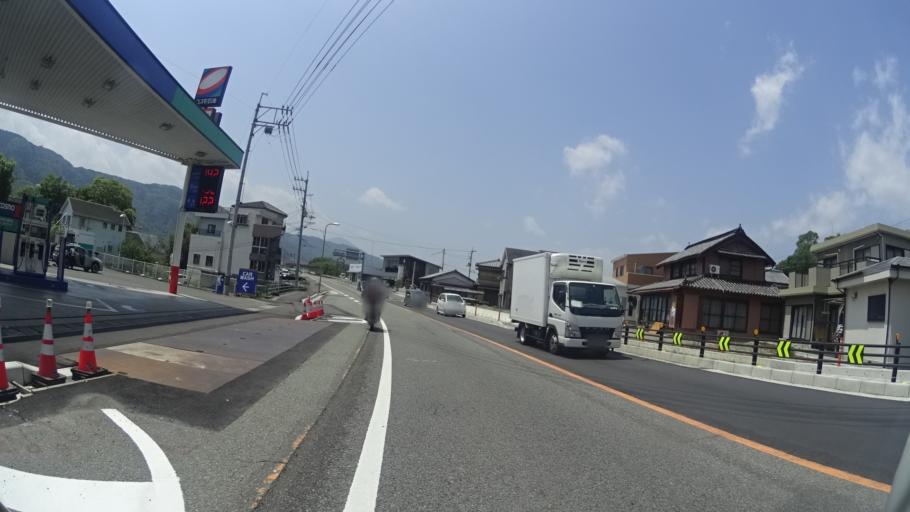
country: JP
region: Tokushima
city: Kamojimacho-jogejima
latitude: 34.0650
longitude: 134.3196
